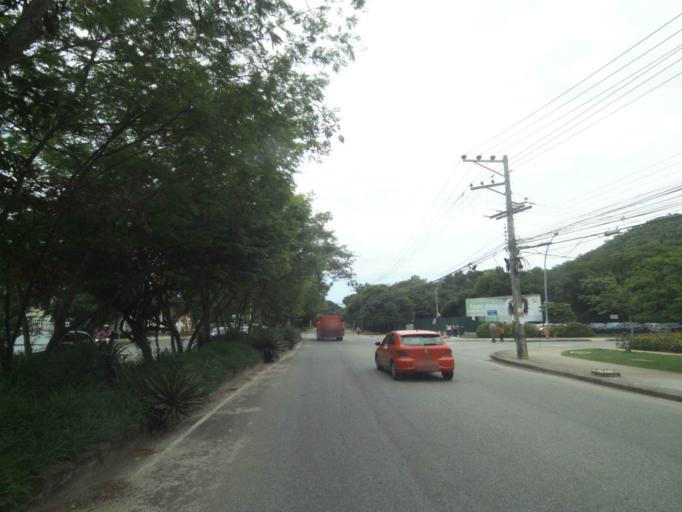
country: BR
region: Rio de Janeiro
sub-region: Nilopolis
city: Nilopolis
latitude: -22.9734
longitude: -43.4143
